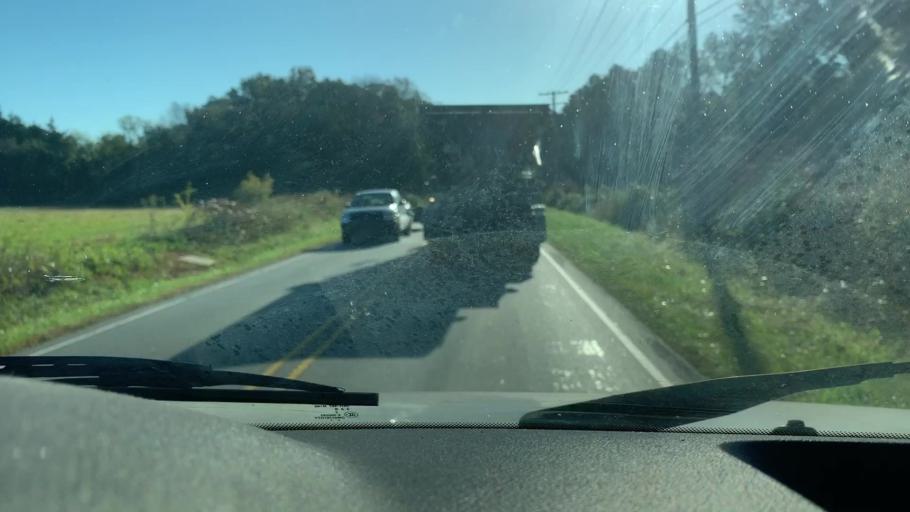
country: US
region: North Carolina
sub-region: Mecklenburg County
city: Huntersville
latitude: 35.4194
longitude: -80.7488
